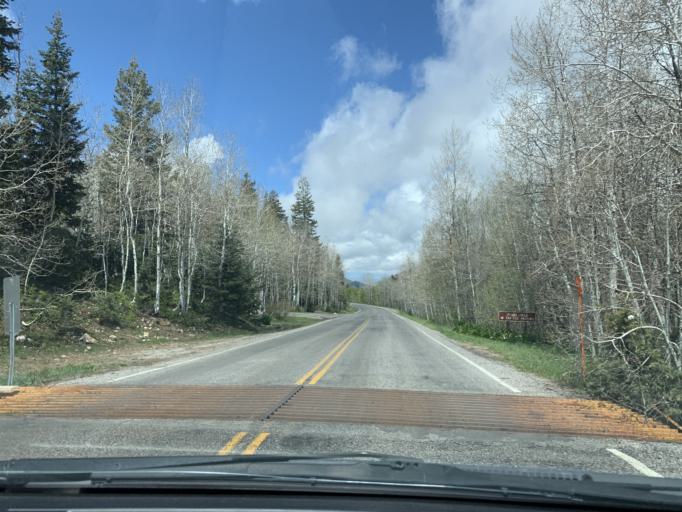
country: US
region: Utah
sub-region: Utah County
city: Woodland Hills
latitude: 39.9400
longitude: -111.6408
